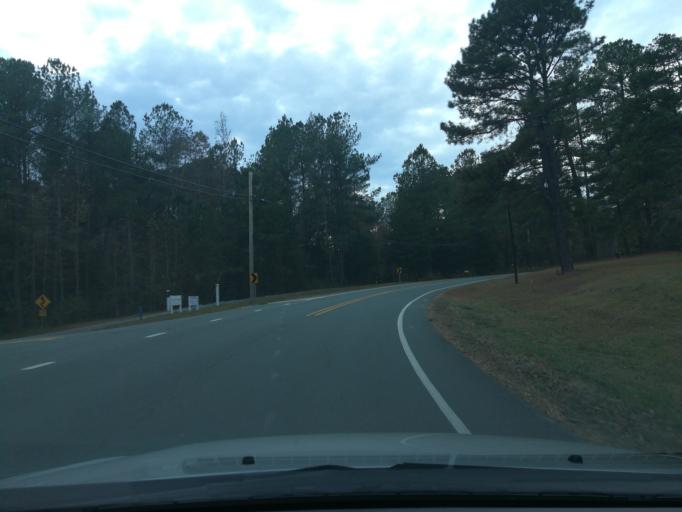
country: US
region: North Carolina
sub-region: Orange County
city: Hillsborough
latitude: 36.0281
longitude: -79.0108
